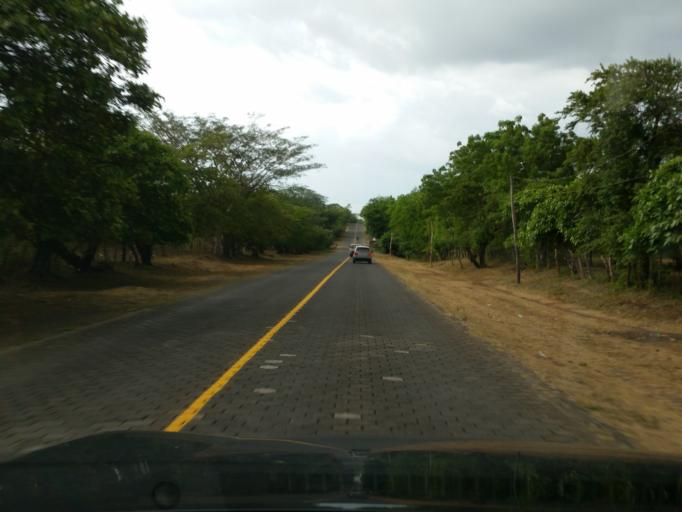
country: NI
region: Managua
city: Carlos Fonseca Amador
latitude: 11.9749
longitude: -86.5143
